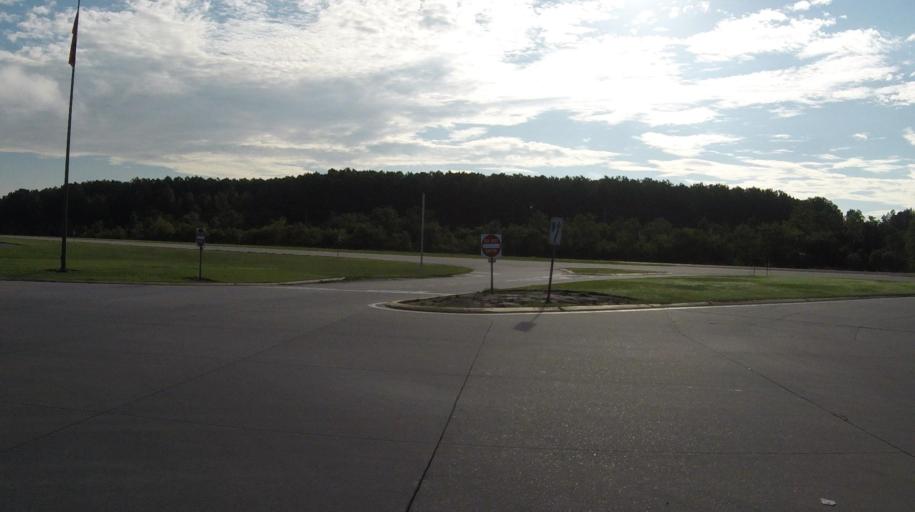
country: US
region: Louisiana
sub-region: Allen Parish
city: Kinder
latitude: 30.5421
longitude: -92.8140
